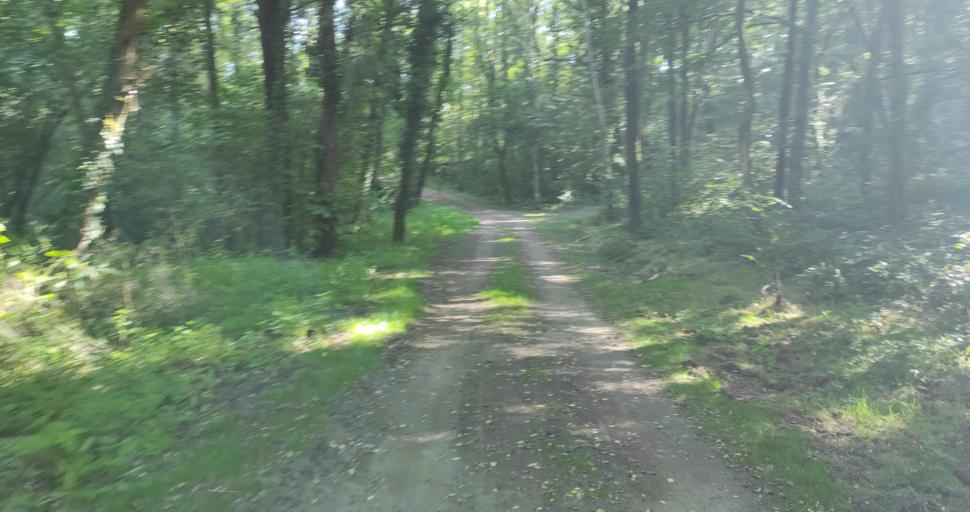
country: FR
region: Midi-Pyrenees
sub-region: Departement de l'Aveyron
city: Cransac
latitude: 44.5306
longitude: 2.2759
